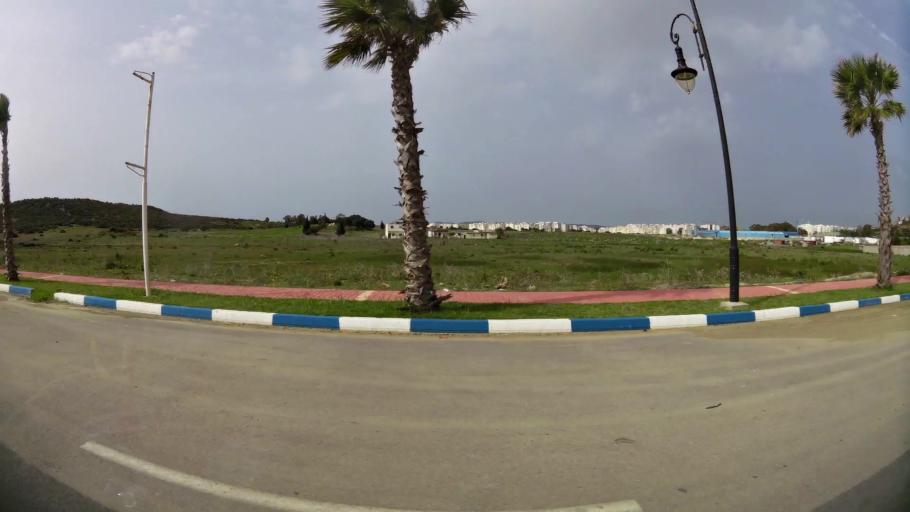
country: MA
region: Tanger-Tetouan
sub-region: Tanger-Assilah
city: Boukhalef
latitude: 35.6970
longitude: -5.9206
